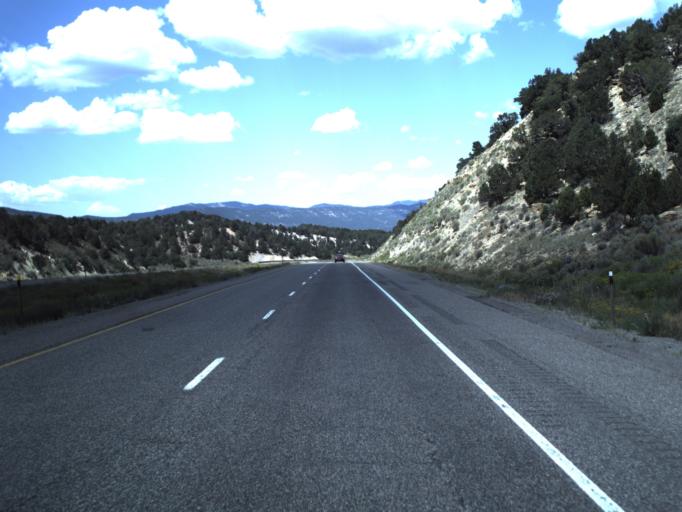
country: US
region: Utah
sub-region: Sevier County
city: Salina
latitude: 38.8189
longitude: -111.5374
